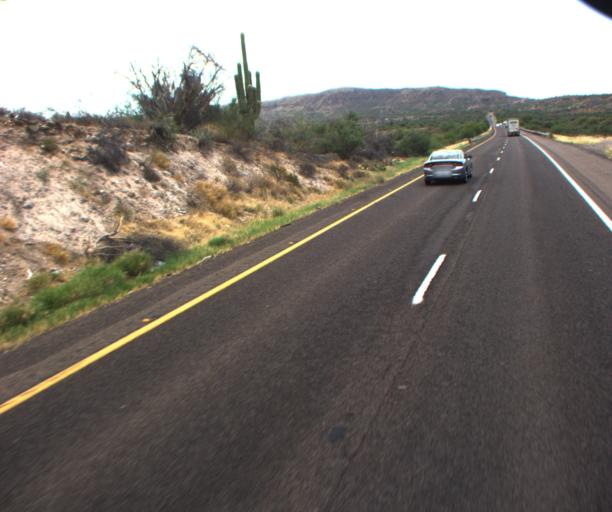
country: US
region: Arizona
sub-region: Yavapai County
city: Black Canyon City
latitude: 34.0113
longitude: -112.1450
